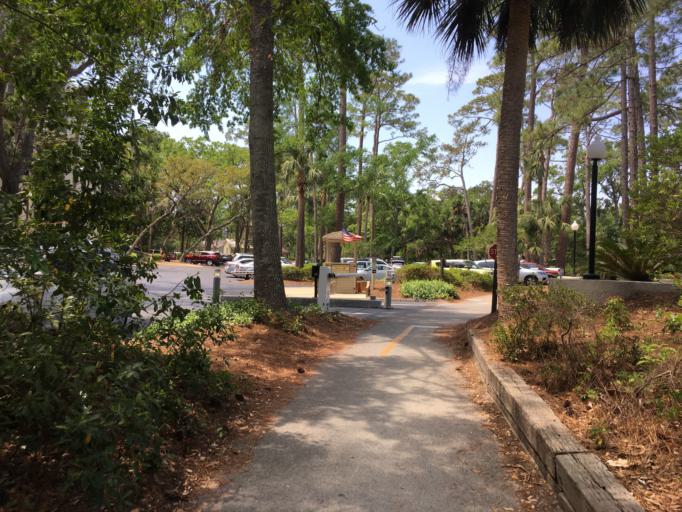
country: US
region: South Carolina
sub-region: Beaufort County
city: Hilton Head Island
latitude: 32.1261
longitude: -80.7877
